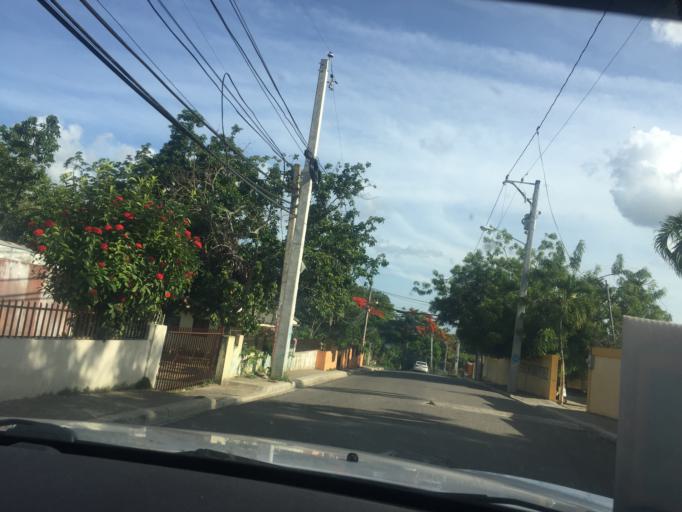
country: DO
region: Santiago
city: Tamboril
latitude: 19.4972
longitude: -70.6345
